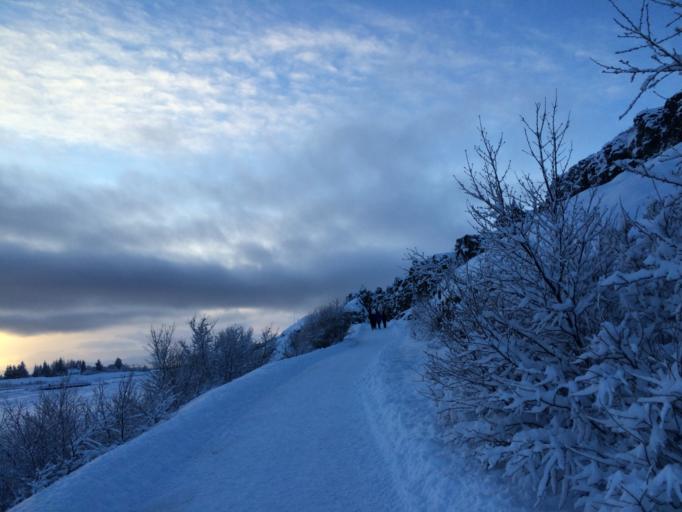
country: IS
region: South
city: Hveragerdi
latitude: 64.2618
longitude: -21.1206
